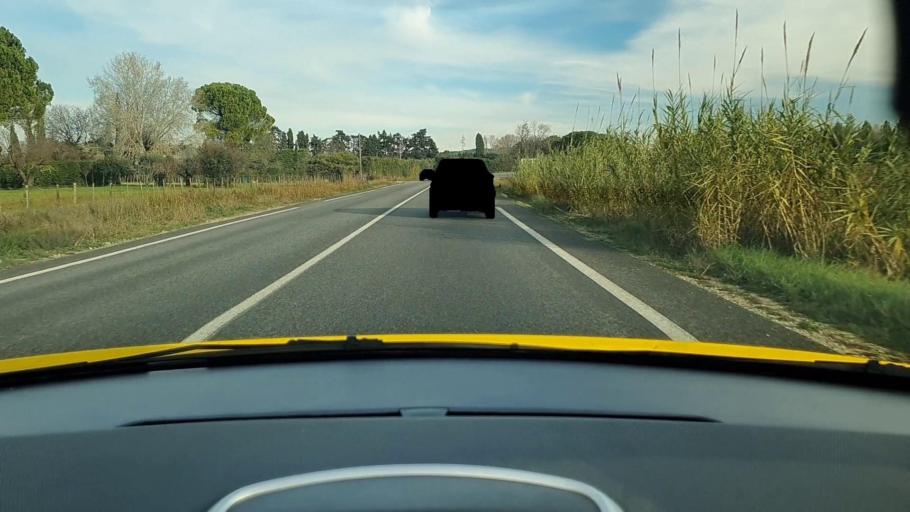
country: FR
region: Languedoc-Roussillon
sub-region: Departement du Gard
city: Beaucaire
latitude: 43.7898
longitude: 4.6277
